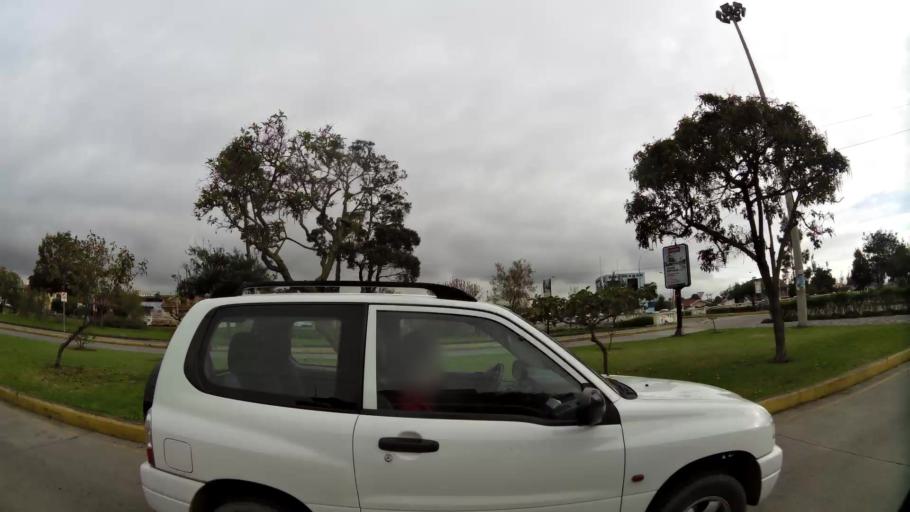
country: EC
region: Azuay
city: Cuenca
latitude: -2.9104
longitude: -78.9942
